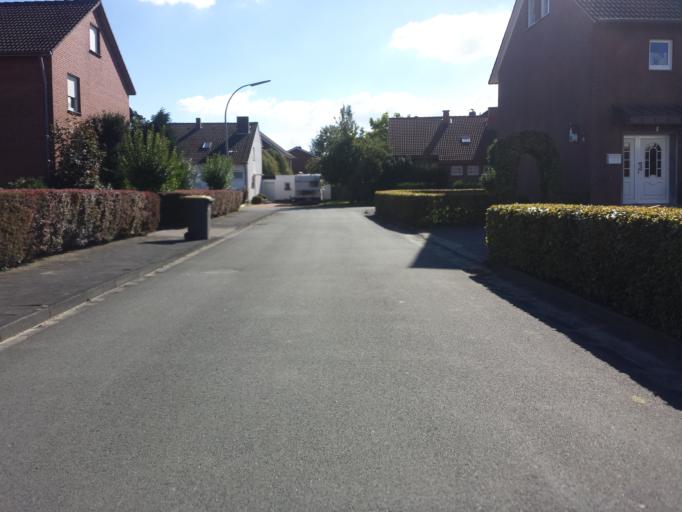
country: DE
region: North Rhine-Westphalia
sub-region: Regierungsbezirk Detmold
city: Langenberg
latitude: 51.7657
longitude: 8.3125
